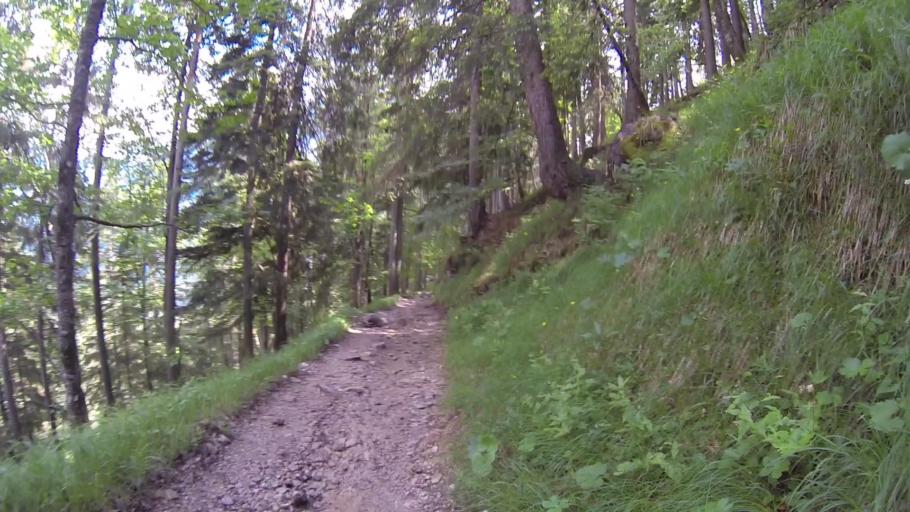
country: DE
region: Bavaria
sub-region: Swabia
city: Halblech
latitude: 47.5292
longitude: 10.8354
